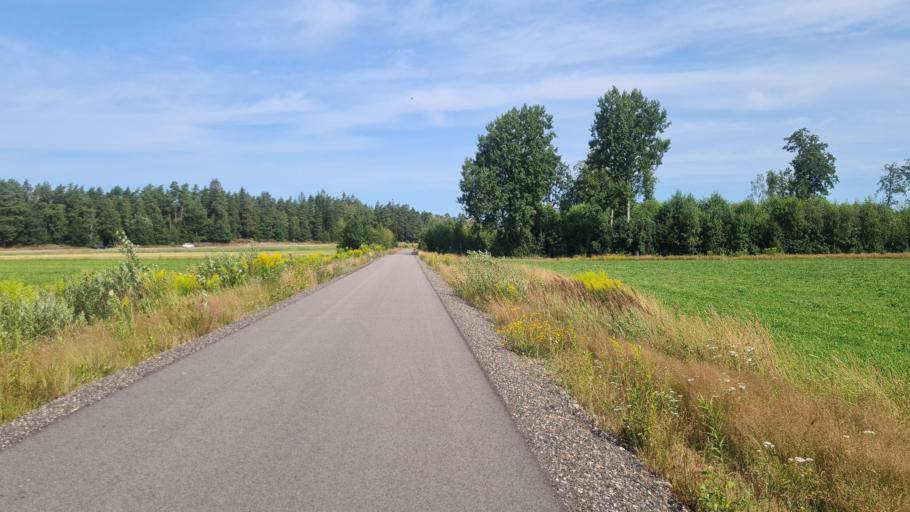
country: SE
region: Kronoberg
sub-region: Ljungby Kommun
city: Ljungby
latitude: 56.8637
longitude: 13.9776
